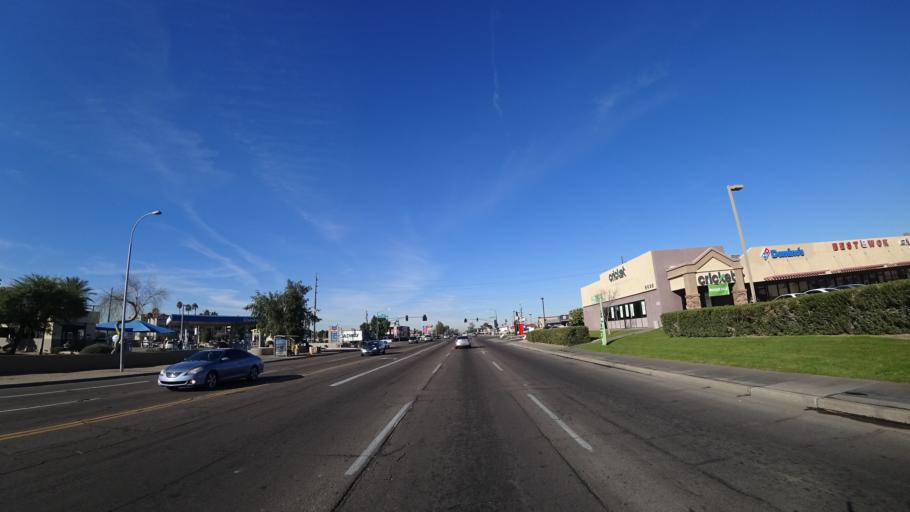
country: US
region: Arizona
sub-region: Maricopa County
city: Glendale
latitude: 33.4660
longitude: -112.1680
